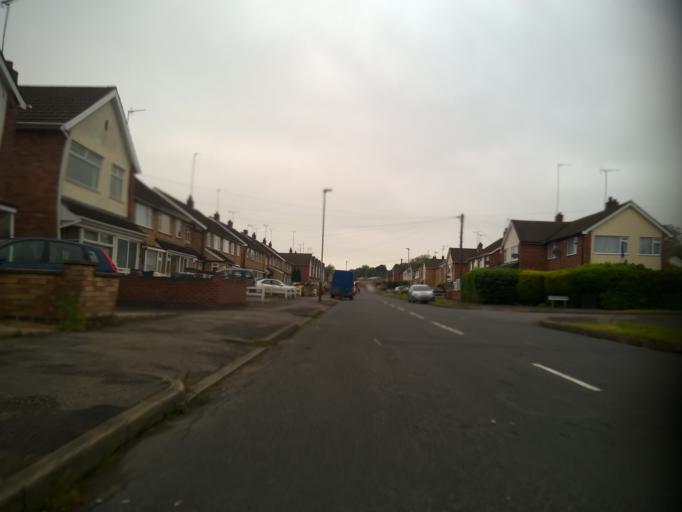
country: GB
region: England
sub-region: City of Leicester
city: Leicester
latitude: 52.6474
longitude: -1.1626
